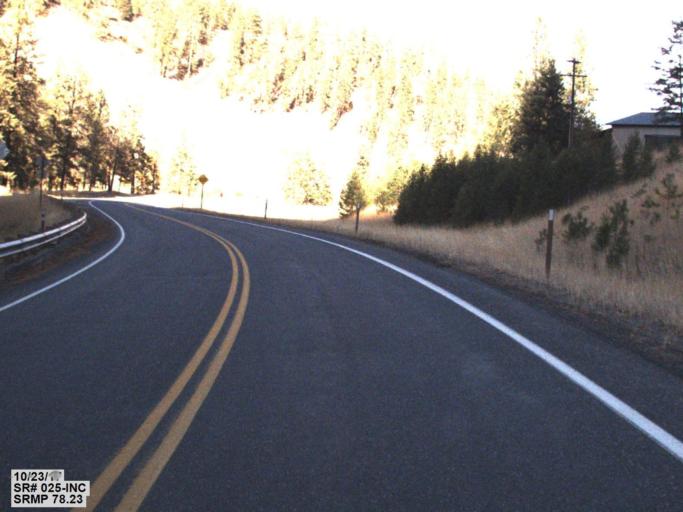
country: US
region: Washington
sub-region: Stevens County
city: Kettle Falls
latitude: 48.5713
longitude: -118.0896
